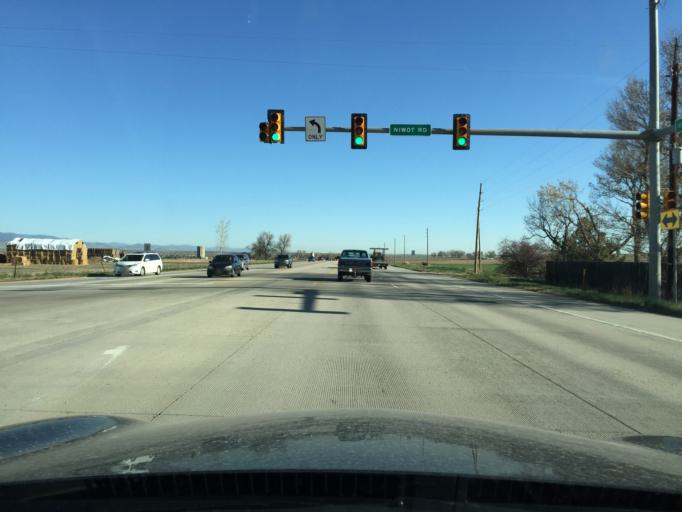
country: US
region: Colorado
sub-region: Boulder County
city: Longmont
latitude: 40.1020
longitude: -105.1028
